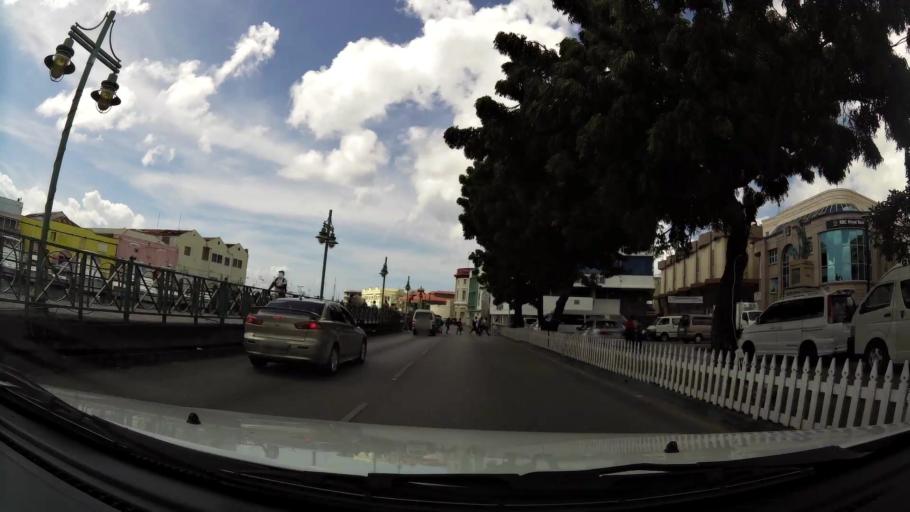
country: BB
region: Saint Michael
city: Bridgetown
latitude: 13.0966
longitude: -59.6143
